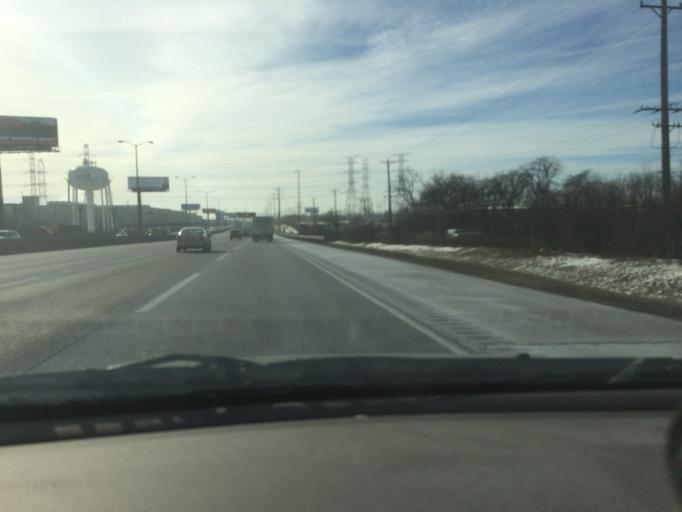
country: US
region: Illinois
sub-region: Cook County
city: Northlake
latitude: 41.9282
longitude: -87.9199
